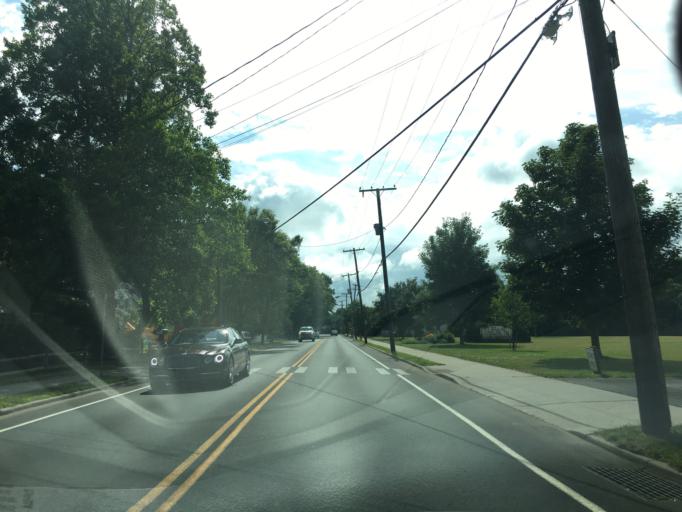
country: US
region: New York
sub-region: Suffolk County
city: Greenport West
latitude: 41.1005
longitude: -72.3685
